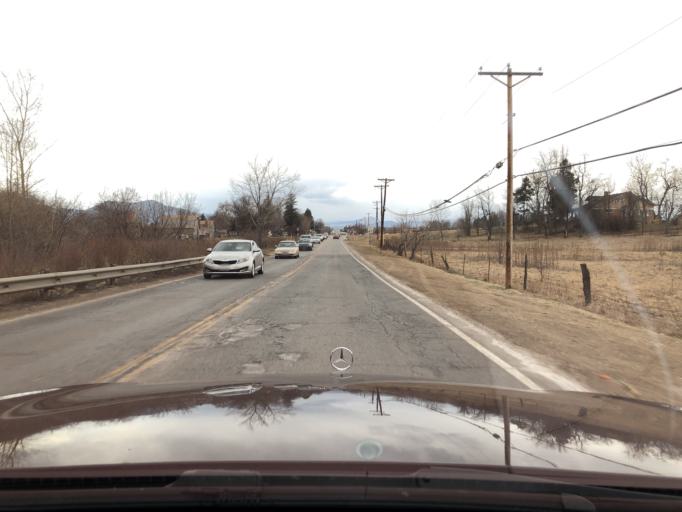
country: US
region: Colorado
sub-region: Boulder County
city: Gunbarrel
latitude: 40.0147
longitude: -105.1714
